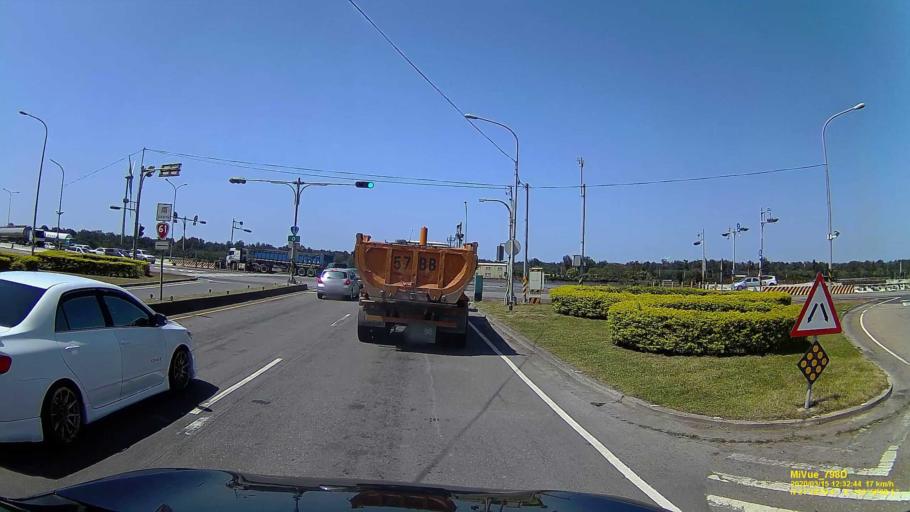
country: TW
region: Taiwan
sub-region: Miaoli
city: Miaoli
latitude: 24.6774
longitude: 120.8441
